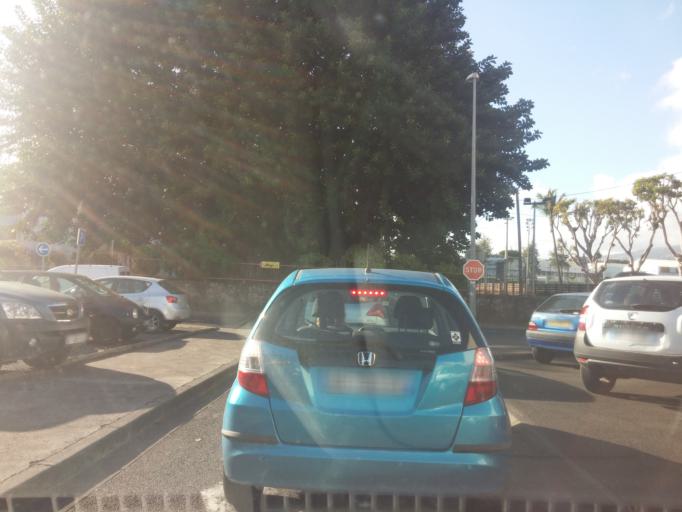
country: RE
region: Reunion
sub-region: Reunion
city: Saint-Denis
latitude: -20.8887
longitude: 55.4662
